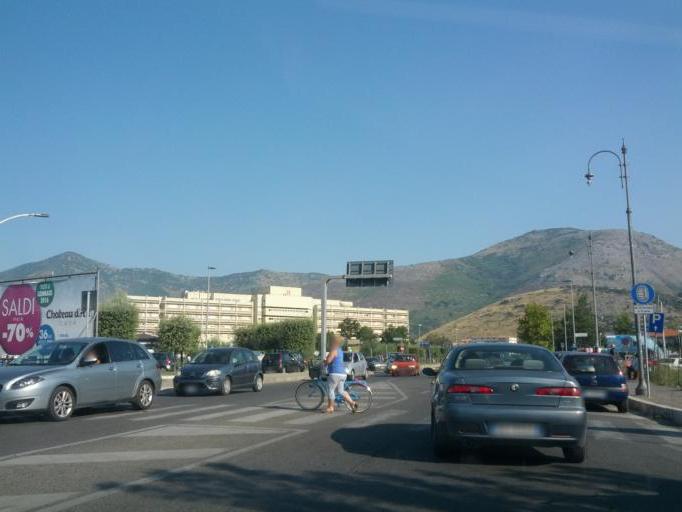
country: IT
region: Latium
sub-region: Provincia di Latina
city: Fondi
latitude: 41.3590
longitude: 13.4173
